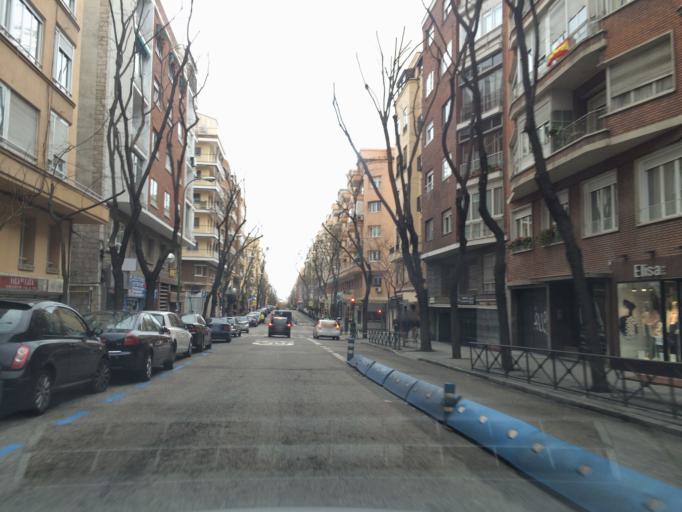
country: ES
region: Madrid
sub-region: Provincia de Madrid
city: Chamberi
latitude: 40.4383
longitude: -3.7129
